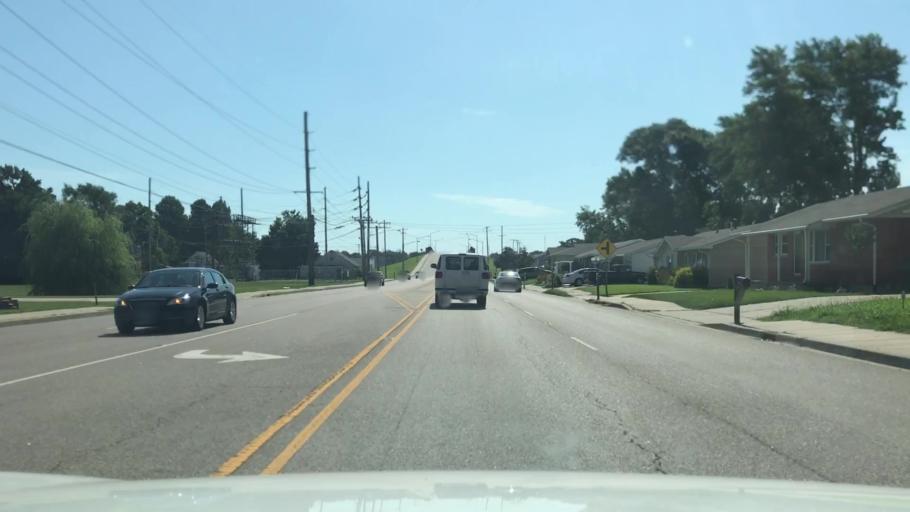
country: US
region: Illinois
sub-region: Madison County
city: Granite City
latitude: 38.7315
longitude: -90.1302
